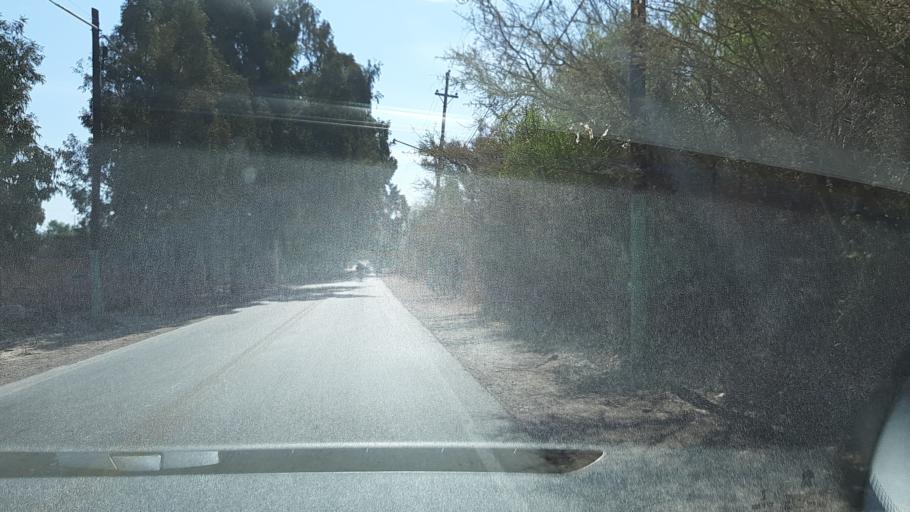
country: AR
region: San Juan
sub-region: Departamento de Rivadavia
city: Rivadavia
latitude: -31.5352
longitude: -68.6176
